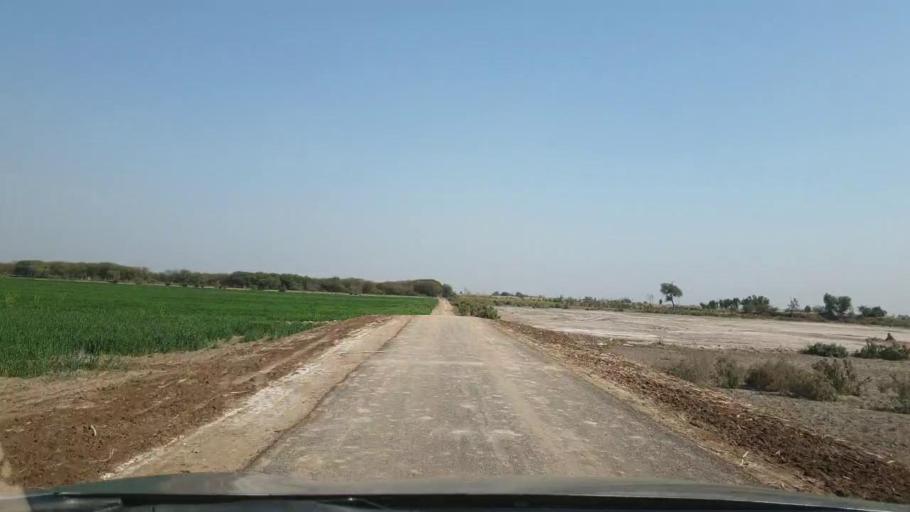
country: PK
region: Sindh
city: Mirpur Khas
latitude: 25.5670
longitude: 68.8896
